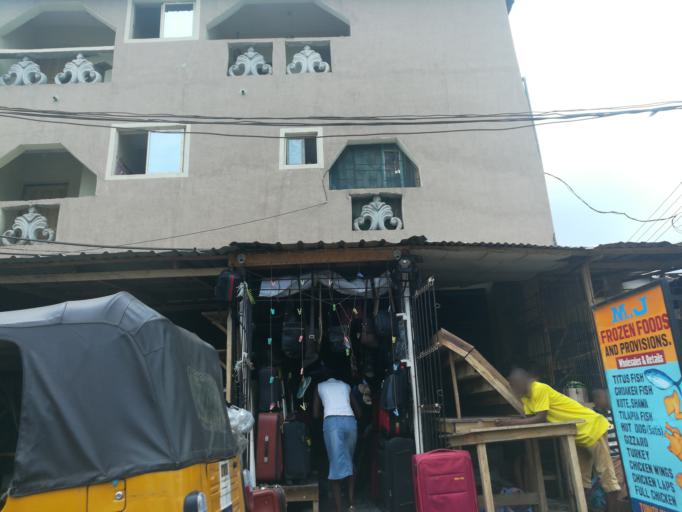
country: NG
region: Lagos
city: Ojota
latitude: 6.5715
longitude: 3.3652
